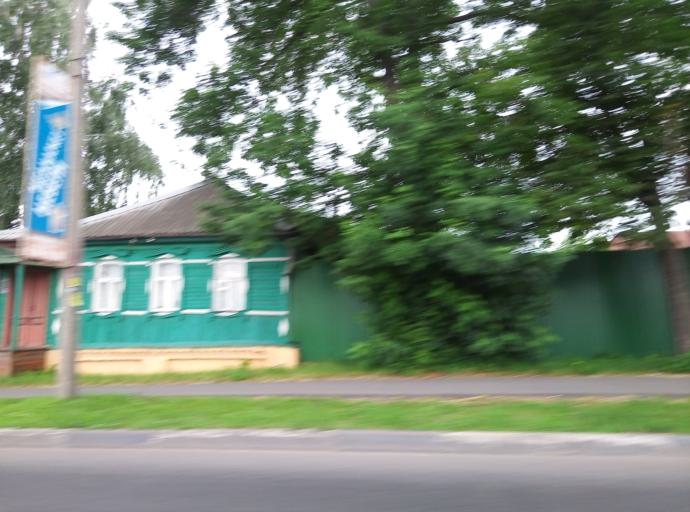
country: RU
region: Kursk
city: Kursk
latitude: 51.7329
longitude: 36.1550
